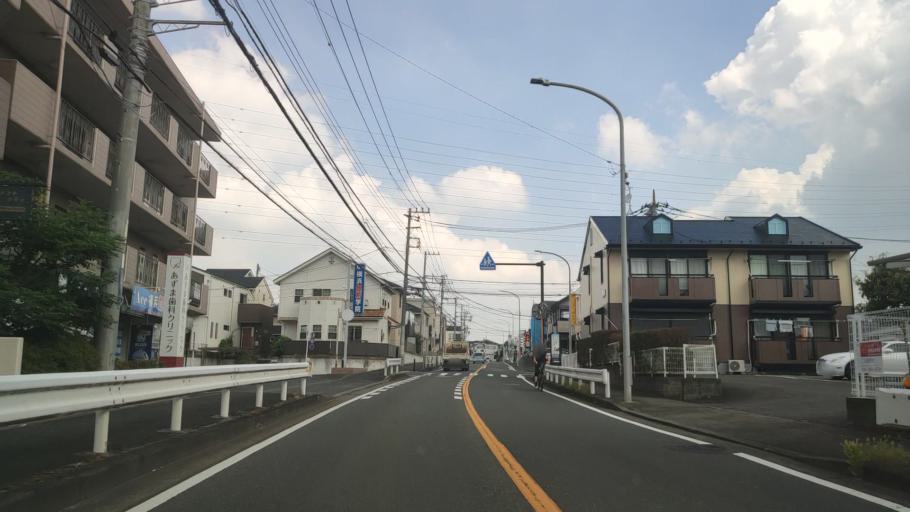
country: JP
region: Kanagawa
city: Minami-rinkan
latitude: 35.4511
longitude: 139.5029
